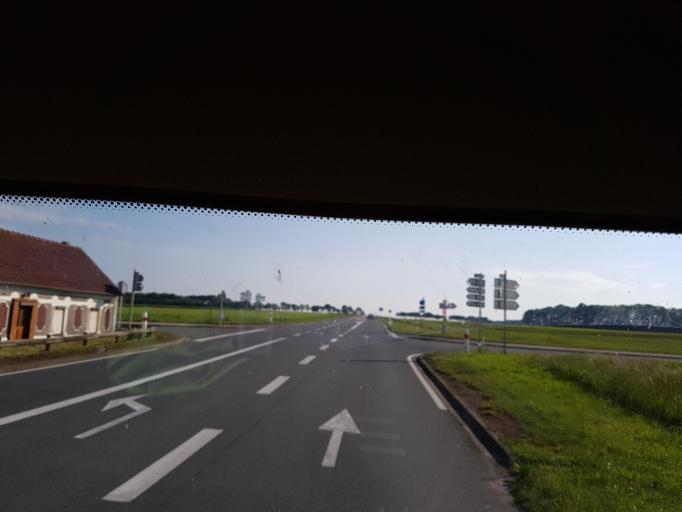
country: FR
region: Picardie
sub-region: Departement de la Somme
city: Crecy-en-Ponthieu
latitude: 50.2138
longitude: 1.9117
